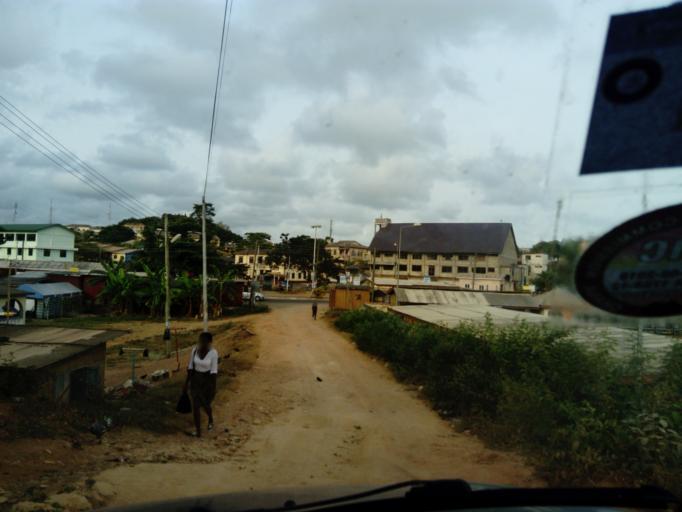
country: GH
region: Central
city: Cape Coast
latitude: 5.1075
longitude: -1.2533
